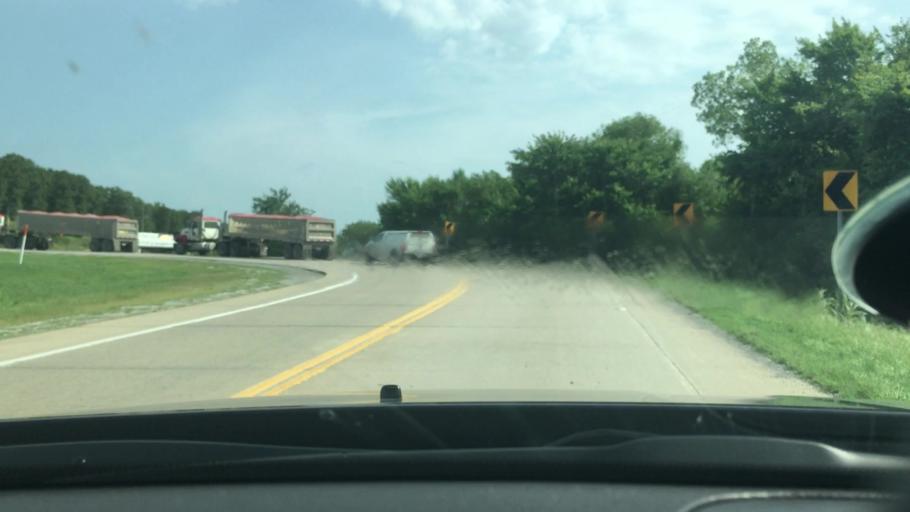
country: US
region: Oklahoma
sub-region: Atoka County
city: Atoka
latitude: 34.4719
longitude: -96.0527
